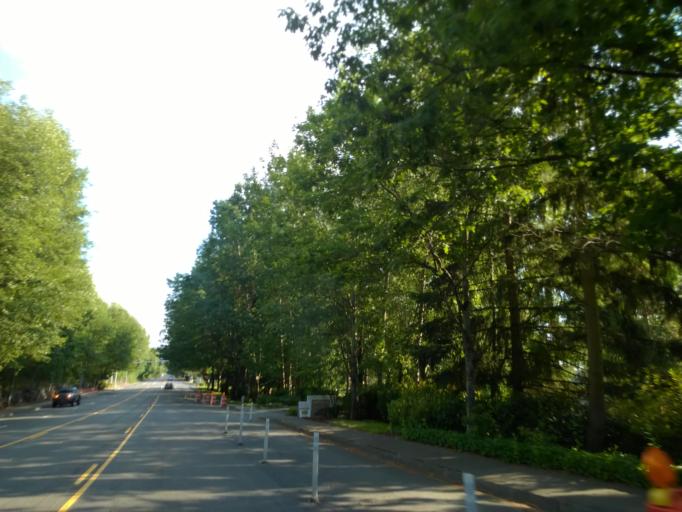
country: US
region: Washington
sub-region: King County
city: Woodinville
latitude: 47.7752
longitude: -122.1802
